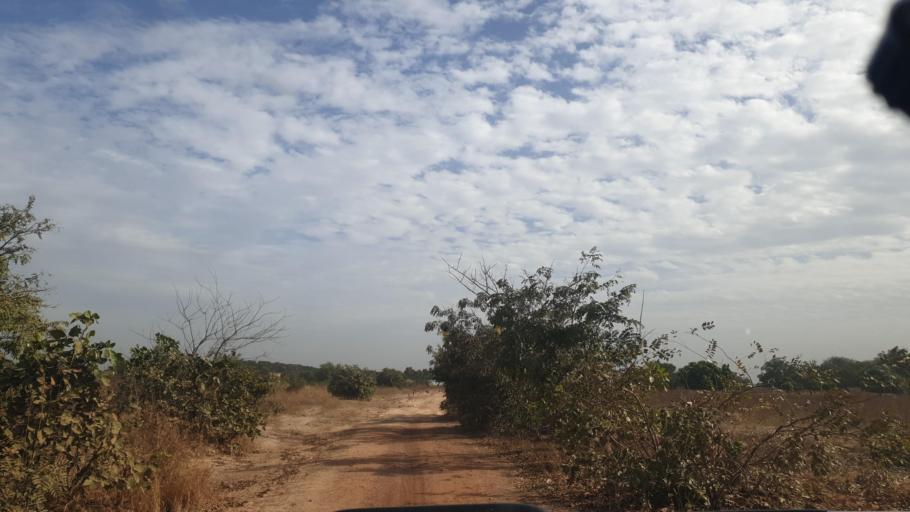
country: ML
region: Sikasso
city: Yanfolila
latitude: 11.4126
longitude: -8.0045
